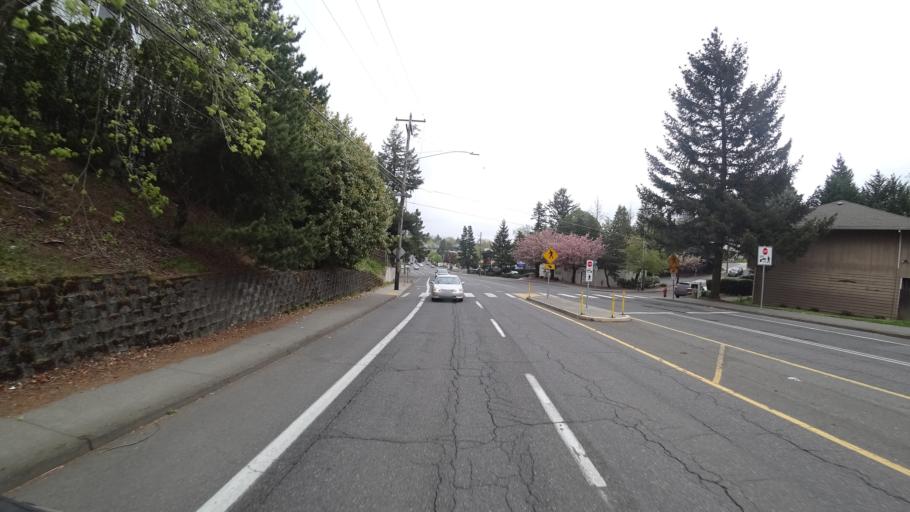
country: US
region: Oregon
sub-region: Washington County
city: Metzger
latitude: 45.4509
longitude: -122.7230
